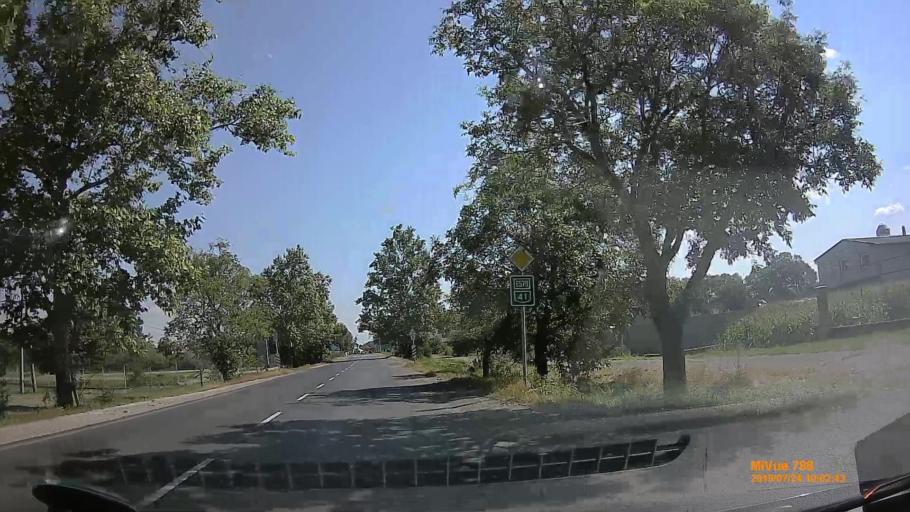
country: HU
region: Szabolcs-Szatmar-Bereg
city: Vasarosnameny
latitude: 48.1140
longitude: 22.3109
